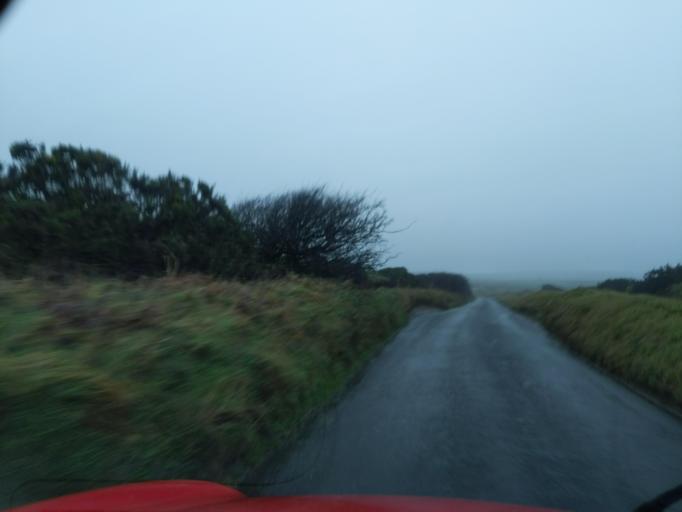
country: GB
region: England
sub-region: Cornwall
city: Camelford
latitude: 50.6544
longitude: -4.7018
